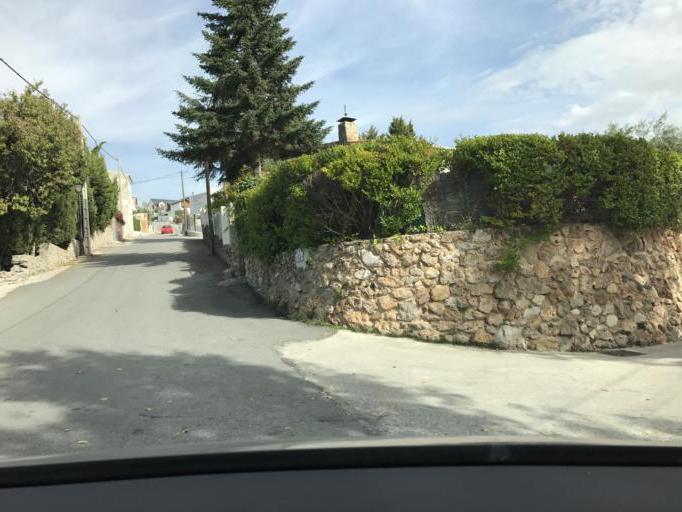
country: ES
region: Andalusia
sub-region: Provincia de Granada
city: Huetor Santillan
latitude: 37.2256
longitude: -3.5159
